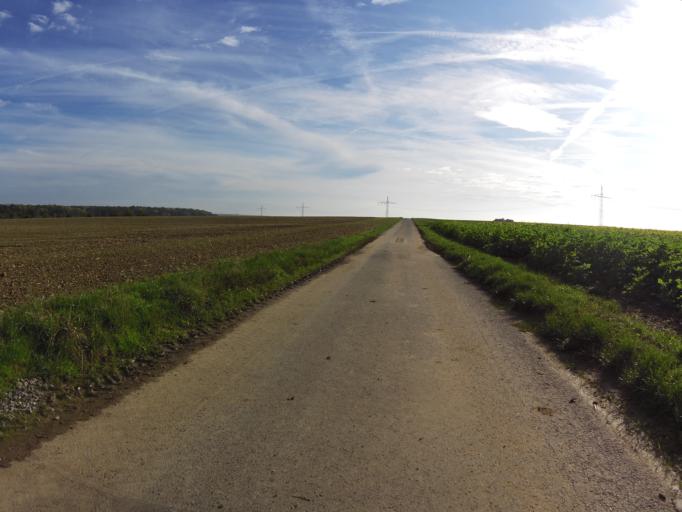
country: DE
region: Bavaria
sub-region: Regierungsbezirk Unterfranken
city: Biebelried
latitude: 49.7260
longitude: 10.0762
